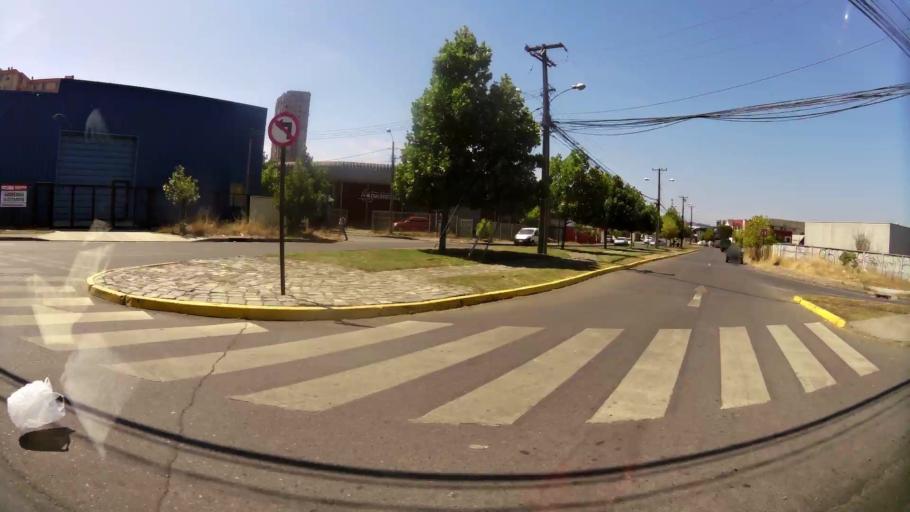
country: CL
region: Biobio
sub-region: Provincia de Concepcion
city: Concepcion
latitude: -36.8140
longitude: -73.0650
